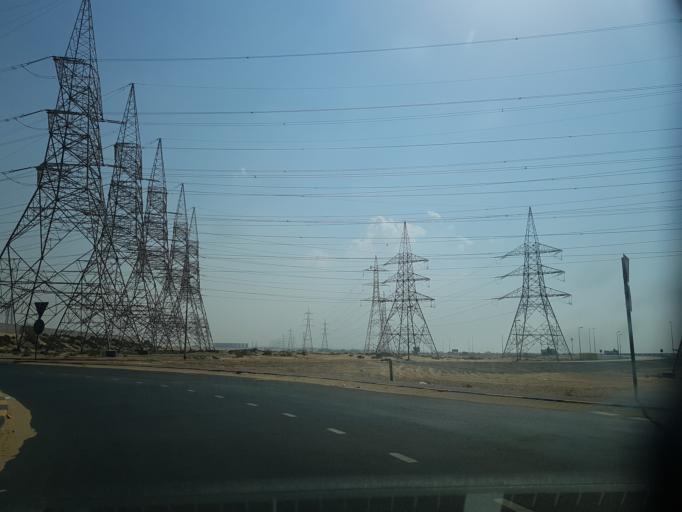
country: AE
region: Ash Shariqah
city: Sharjah
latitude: 25.2863
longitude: 55.5906
